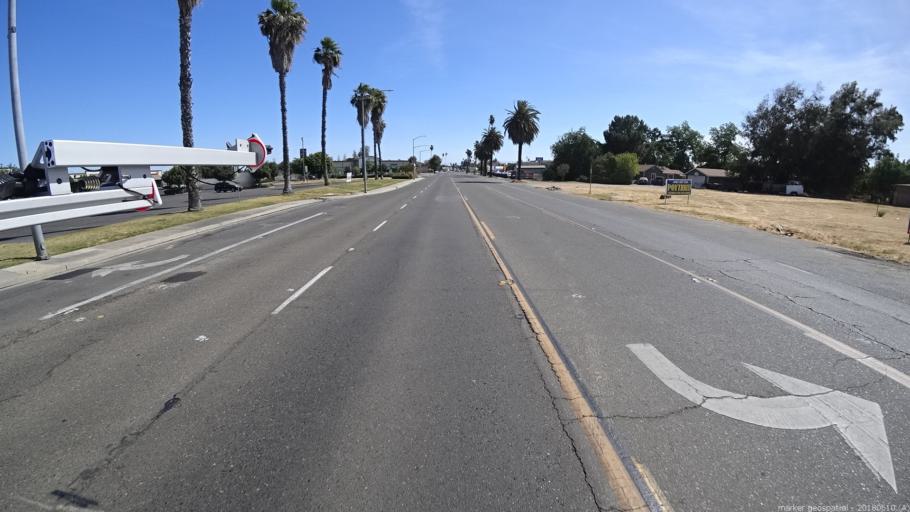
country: US
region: California
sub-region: Madera County
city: Chowchilla
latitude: 37.1105
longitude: -120.2744
